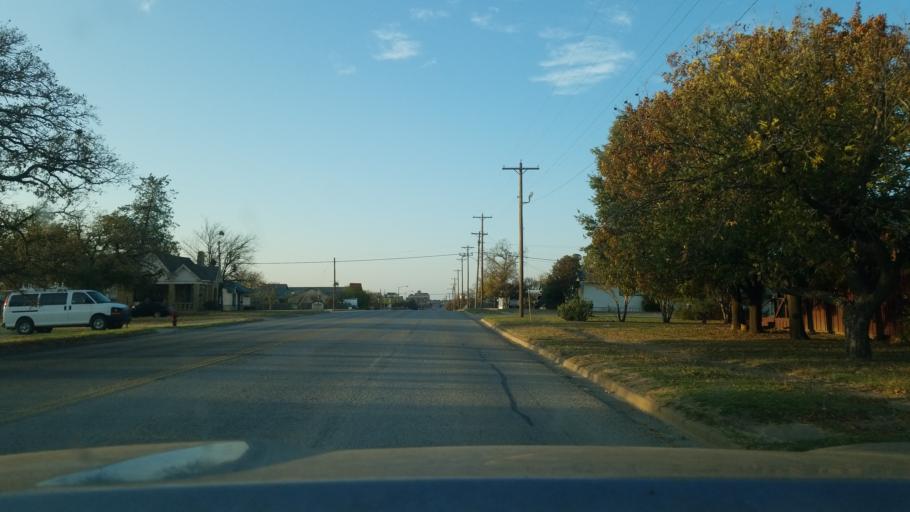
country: US
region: Texas
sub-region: Eastland County
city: Cisco
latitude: 32.3806
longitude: -98.9744
